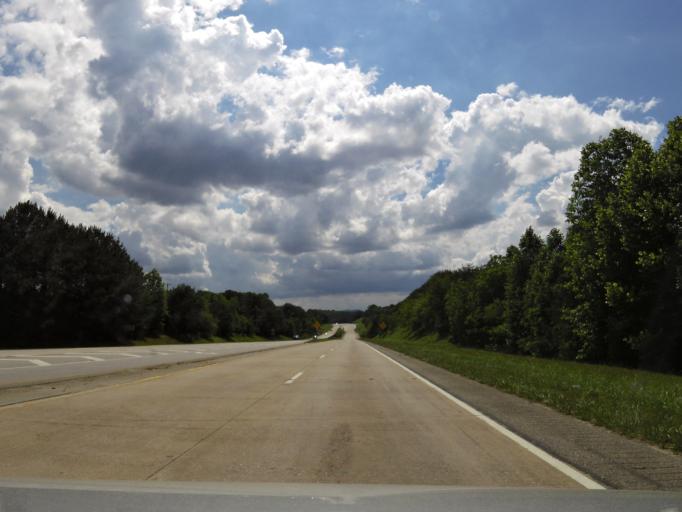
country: US
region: Georgia
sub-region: Union County
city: Blairsville
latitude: 34.8688
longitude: -83.9776
